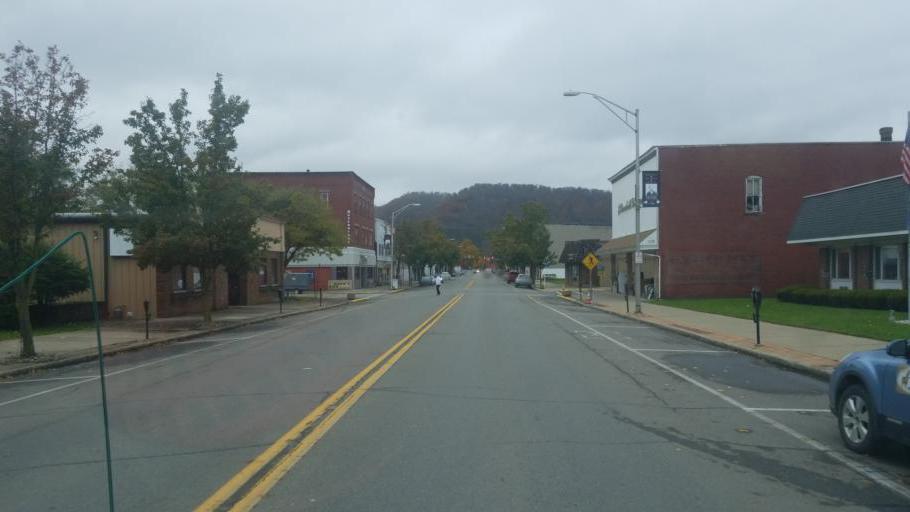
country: US
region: Pennsylvania
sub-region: Cameron County
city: Emporium
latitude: 41.5117
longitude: -78.2348
